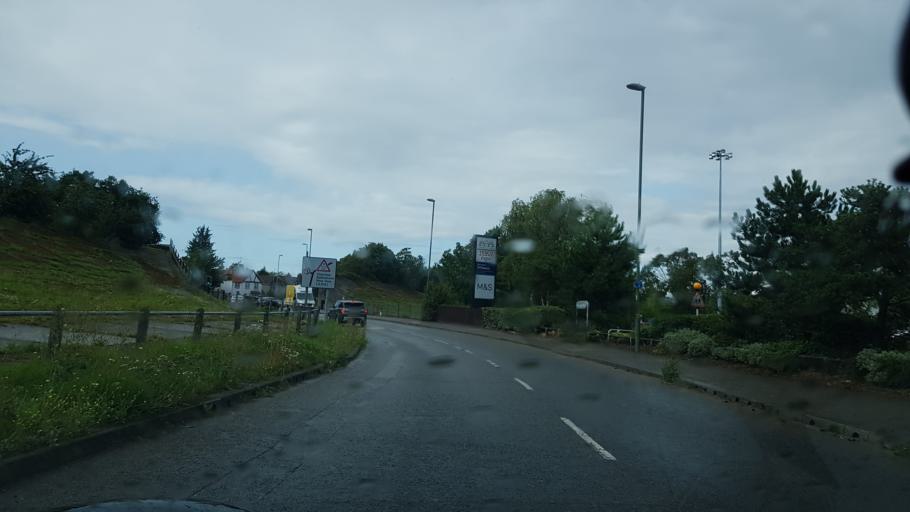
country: GB
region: England
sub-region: Surrey
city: Byfleet
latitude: 51.3441
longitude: -0.4766
